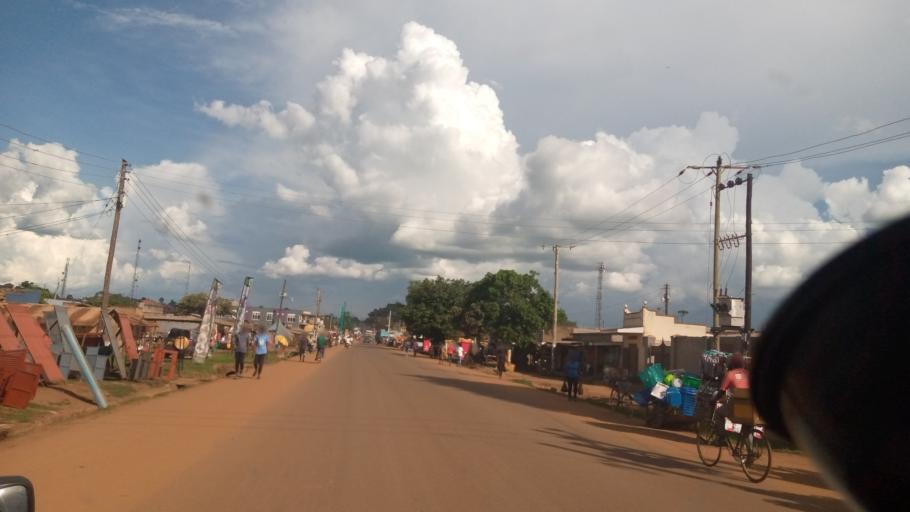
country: UG
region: Northern Region
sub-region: Lira District
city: Lira
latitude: 2.2433
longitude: 32.8871
